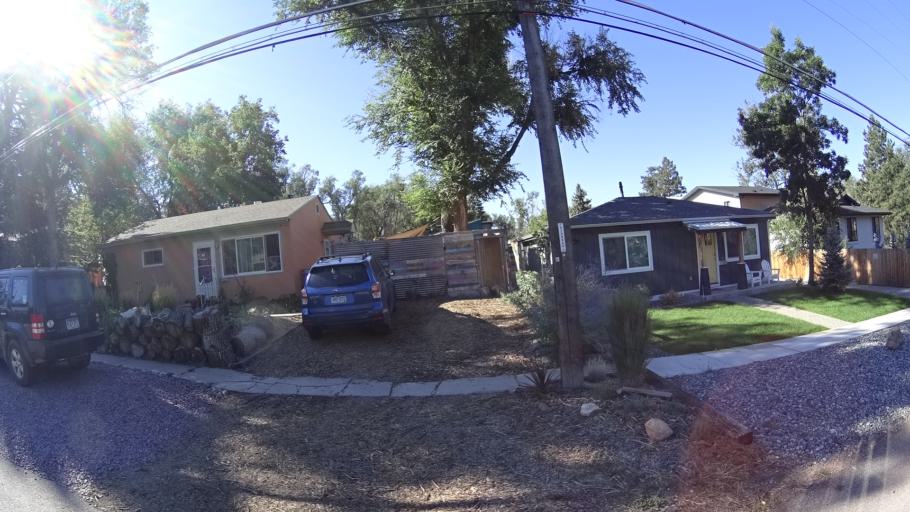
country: US
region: Colorado
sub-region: El Paso County
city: Colorado Springs
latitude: 38.8488
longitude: -104.8094
